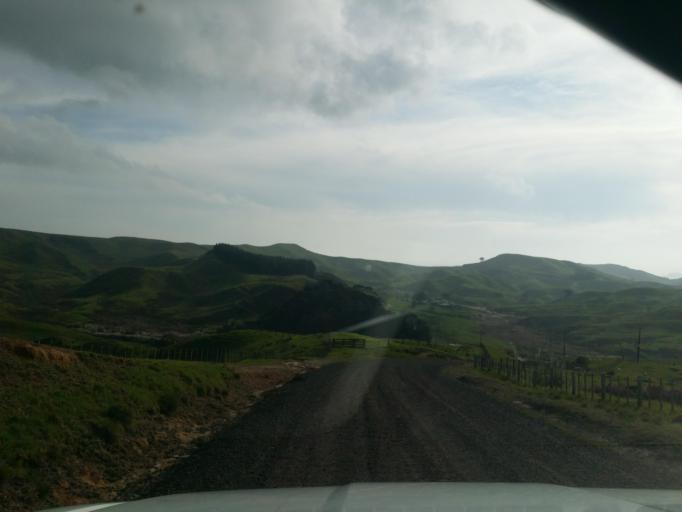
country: NZ
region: Northland
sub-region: Kaipara District
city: Dargaville
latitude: -35.8662
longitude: 173.7317
